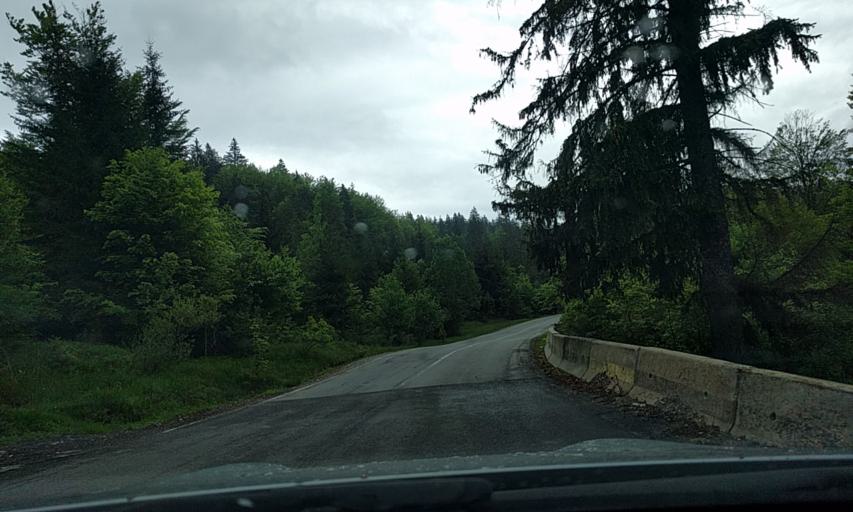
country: RO
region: Prahova
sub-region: Oras Sinaia
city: Sinaia
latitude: 45.3007
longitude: 25.5191
